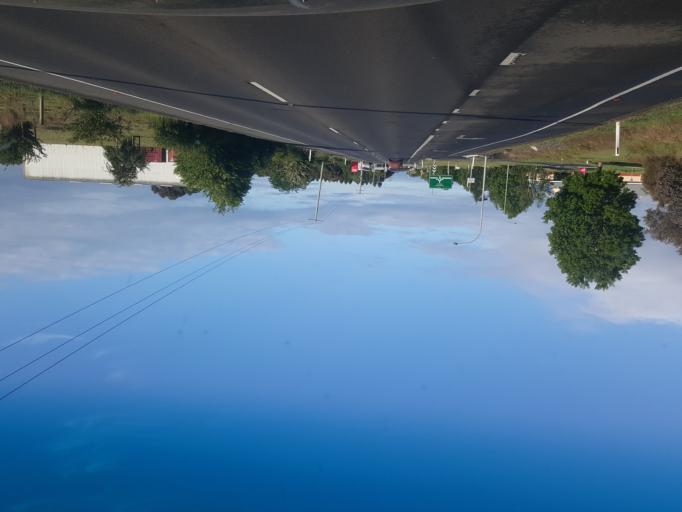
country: AU
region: Tasmania
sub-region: Northern Midlands
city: Perth
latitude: -41.5384
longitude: 147.1981
